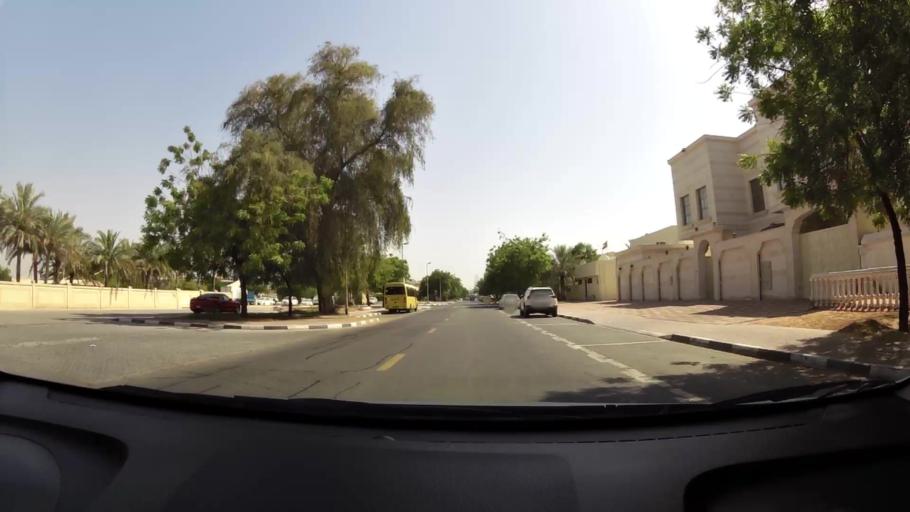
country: AE
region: Ash Shariqah
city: Sharjah
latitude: 25.2667
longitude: 55.3724
